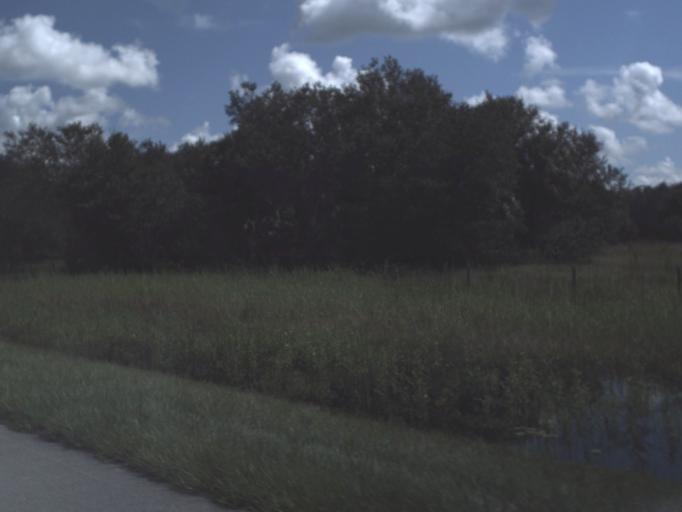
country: US
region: Florida
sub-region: Hendry County
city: Port LaBelle
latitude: 26.8586
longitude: -81.3729
